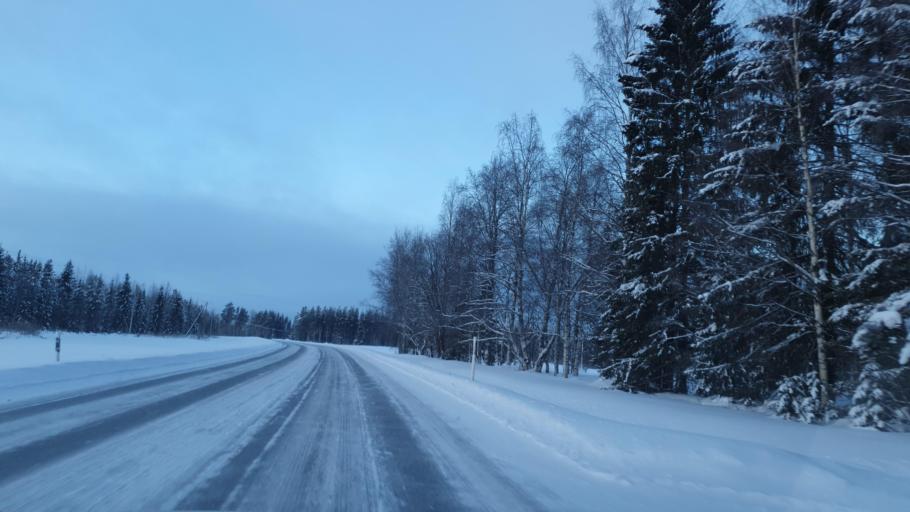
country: FI
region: Kainuu
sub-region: Kajaani
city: Kajaani
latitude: 64.4345
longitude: 27.5696
